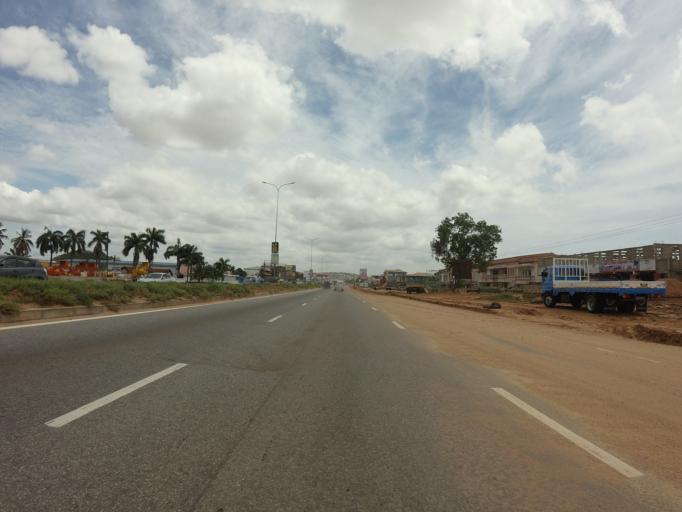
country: GH
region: Greater Accra
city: Gbawe
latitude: 5.5493
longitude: -0.3339
